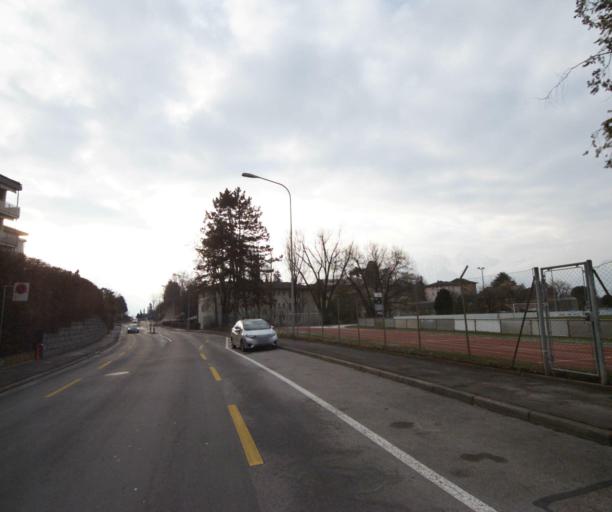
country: CH
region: Vaud
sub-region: Riviera-Pays-d'Enhaut District
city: La Tour-de-Peilz
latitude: 46.4550
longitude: 6.8671
